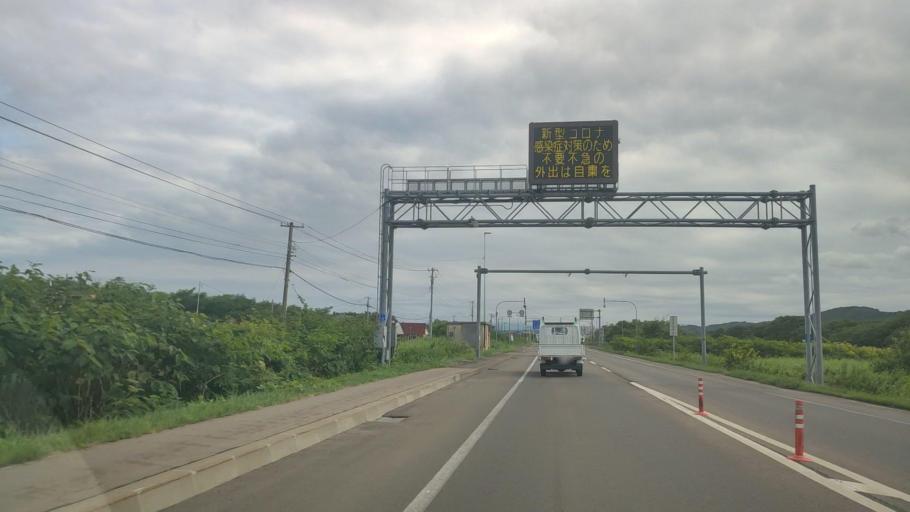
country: JP
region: Hokkaido
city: Niseko Town
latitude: 42.4433
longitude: 140.3269
